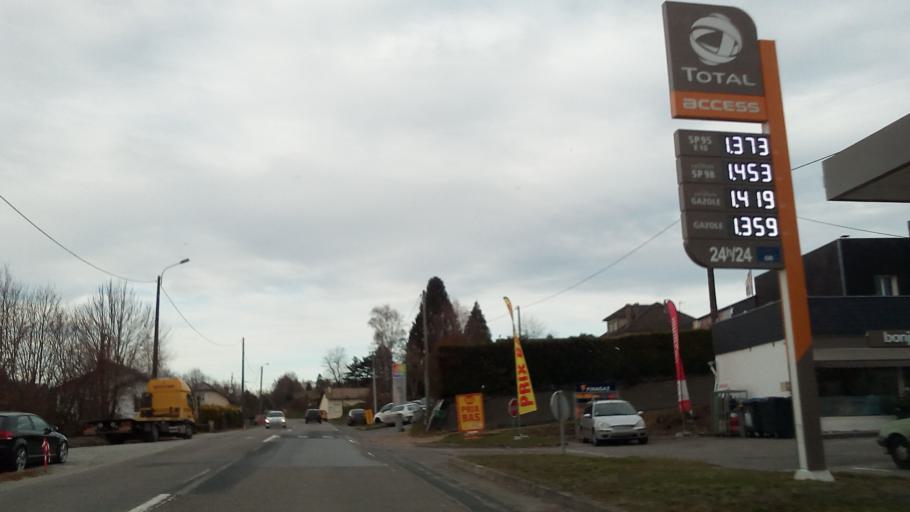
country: FR
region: Limousin
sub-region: Departement de la Correze
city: Naves
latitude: 45.3159
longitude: 1.7704
